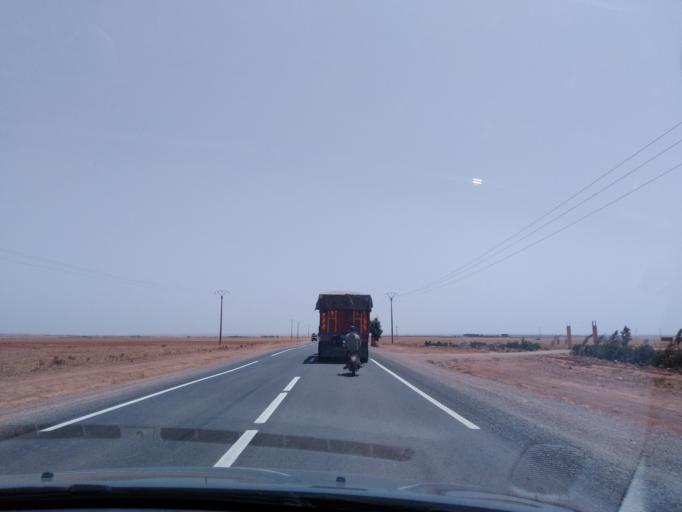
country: MA
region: Doukkala-Abda
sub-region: Safi
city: Youssoufia
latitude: 32.1010
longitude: -8.6994
